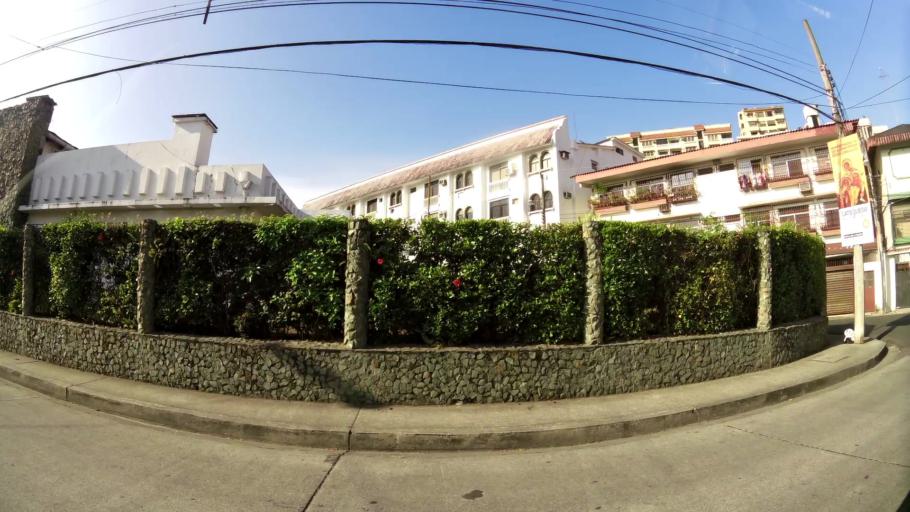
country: EC
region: Guayas
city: Guayaquil
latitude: -2.1622
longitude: -79.9052
